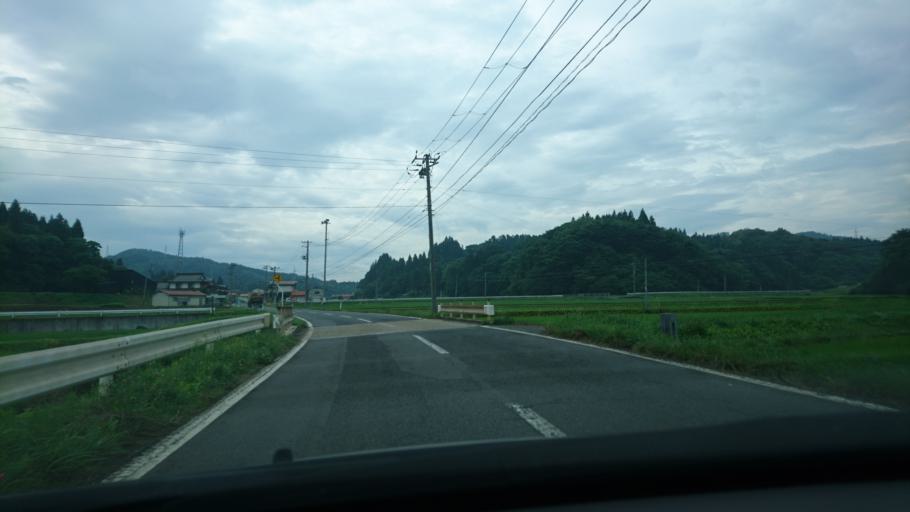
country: JP
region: Iwate
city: Ichinoseki
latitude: 38.9044
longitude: 141.4239
